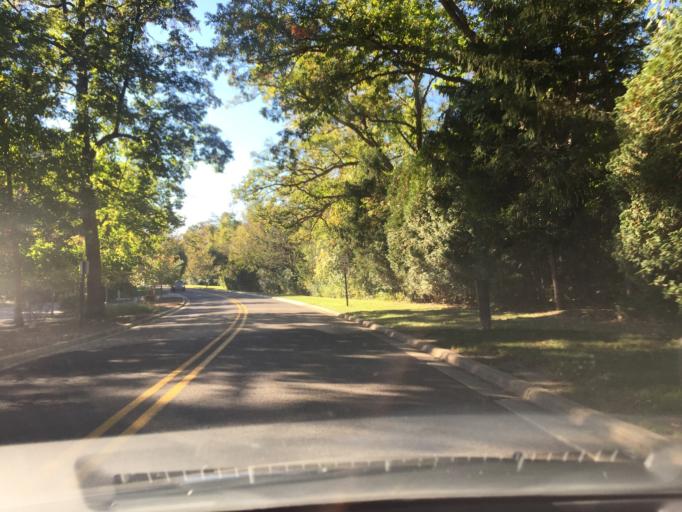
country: US
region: Michigan
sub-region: Oakland County
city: Bloomfield Hills
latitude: 42.5748
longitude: -83.2471
